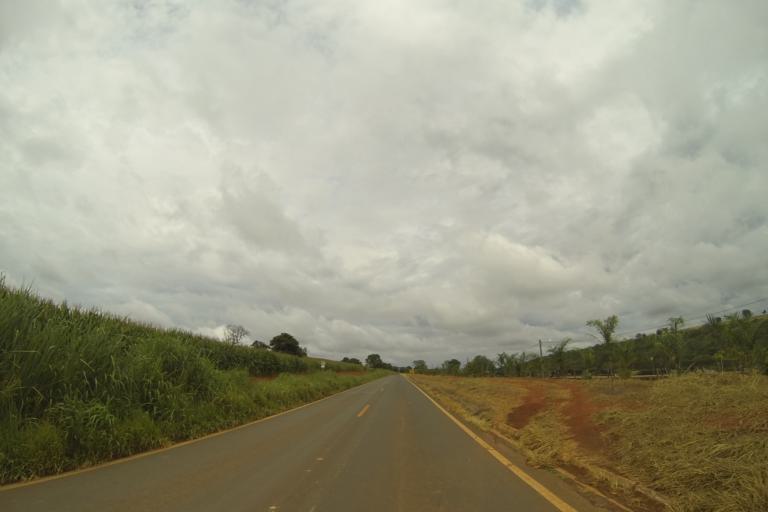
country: BR
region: Minas Gerais
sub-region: Bambui
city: Bambui
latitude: -20.1017
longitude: -46.1045
